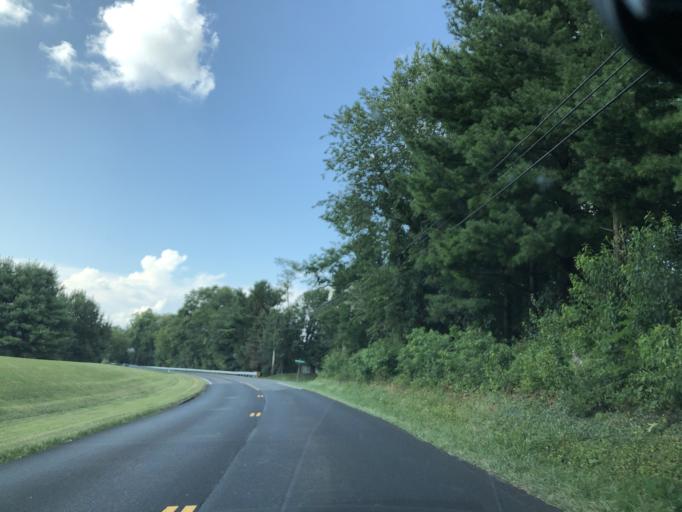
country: US
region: Maryland
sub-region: Carroll County
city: Mount Airy
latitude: 39.4015
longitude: -77.1782
